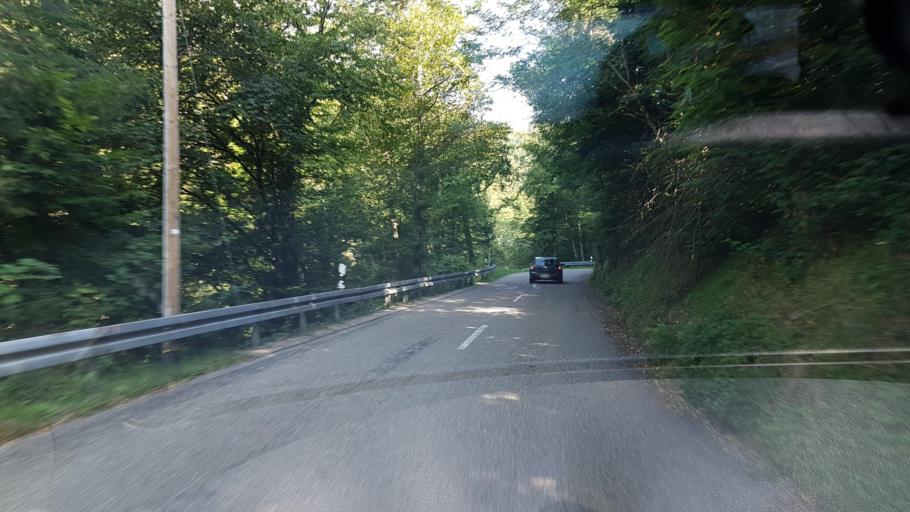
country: DE
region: Baden-Wuerttemberg
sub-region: Freiburg Region
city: Gorwihl
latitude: 47.6269
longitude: 8.0937
